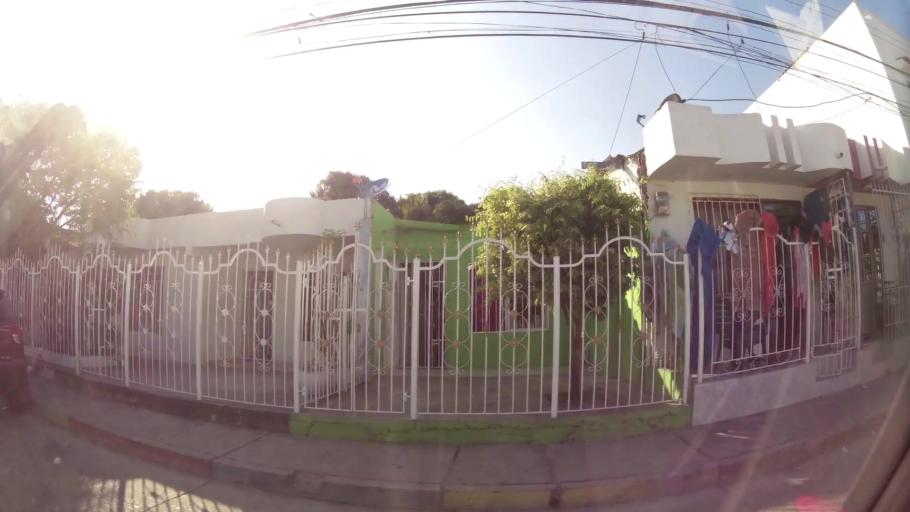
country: CO
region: Bolivar
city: Cartagena
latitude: 10.4042
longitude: -75.4861
